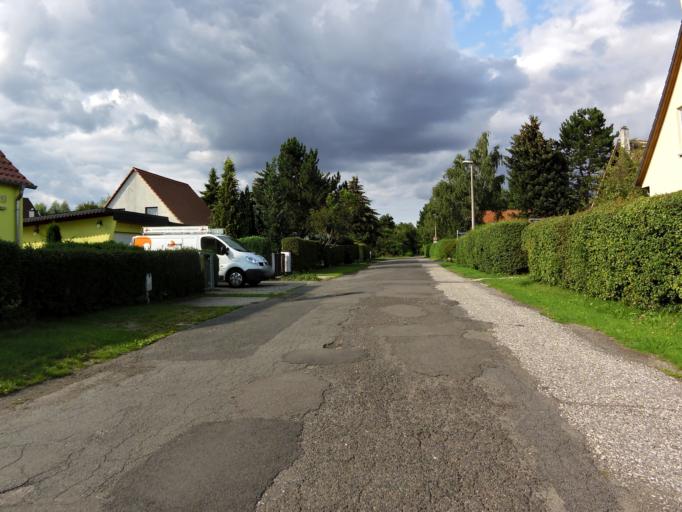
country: DE
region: Saxony
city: Rackwitz
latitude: 51.3844
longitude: 12.4008
